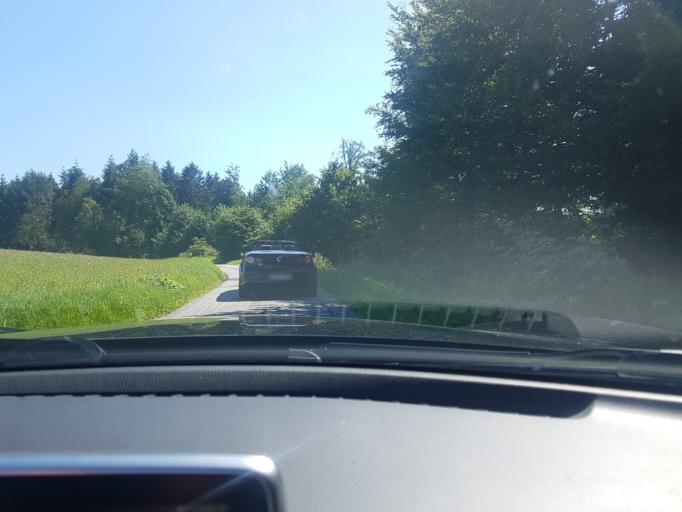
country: DE
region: Baden-Wuerttemberg
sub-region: Karlsruhe Region
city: Reichartshausen
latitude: 49.3900
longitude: 8.9129
